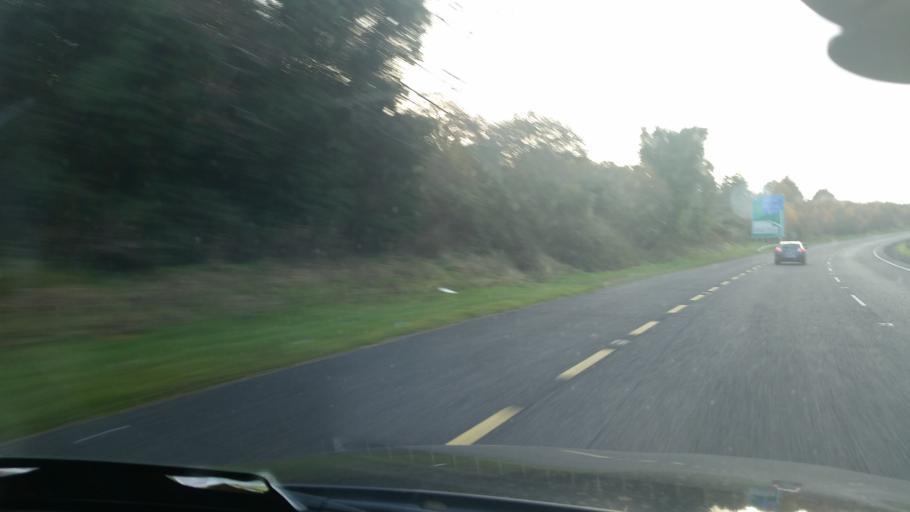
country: IE
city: Newtownmountkennedy
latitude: 53.0567
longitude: -6.0916
